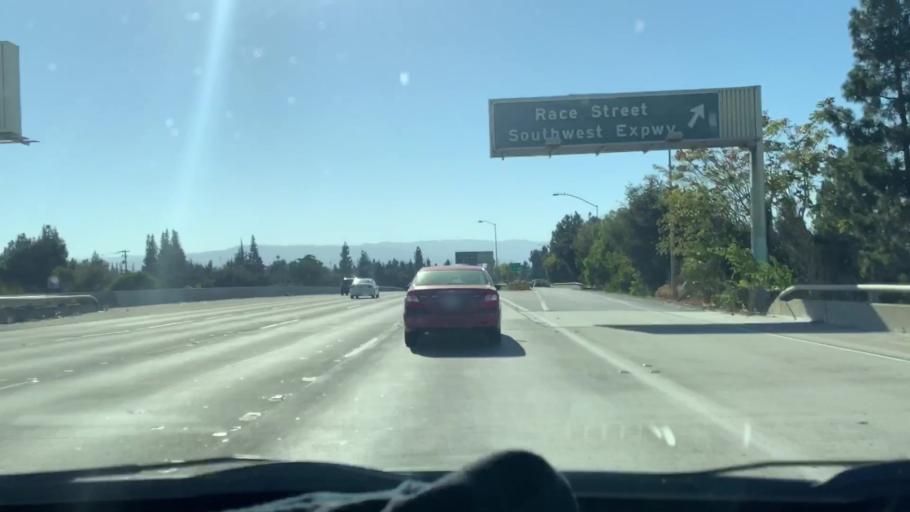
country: US
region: California
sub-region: Santa Clara County
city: Buena Vista
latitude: 37.3169
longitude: -121.9057
